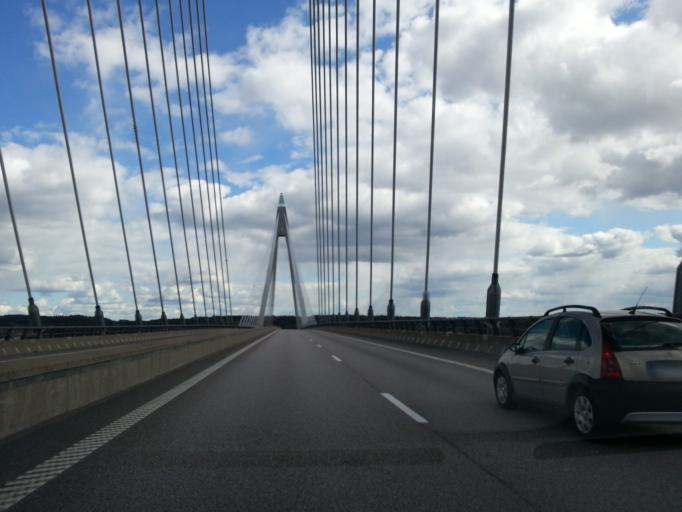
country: SE
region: Vaestra Goetaland
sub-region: Uddevalla Kommun
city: Uddevalla
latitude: 58.3268
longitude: 11.8415
